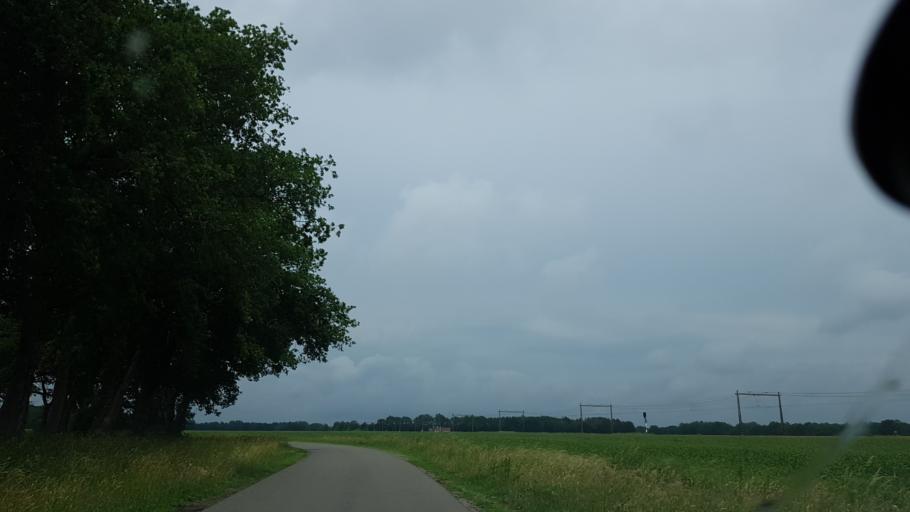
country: NL
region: Drenthe
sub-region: Gemeente Assen
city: Assen
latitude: 53.0216
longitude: 6.6058
